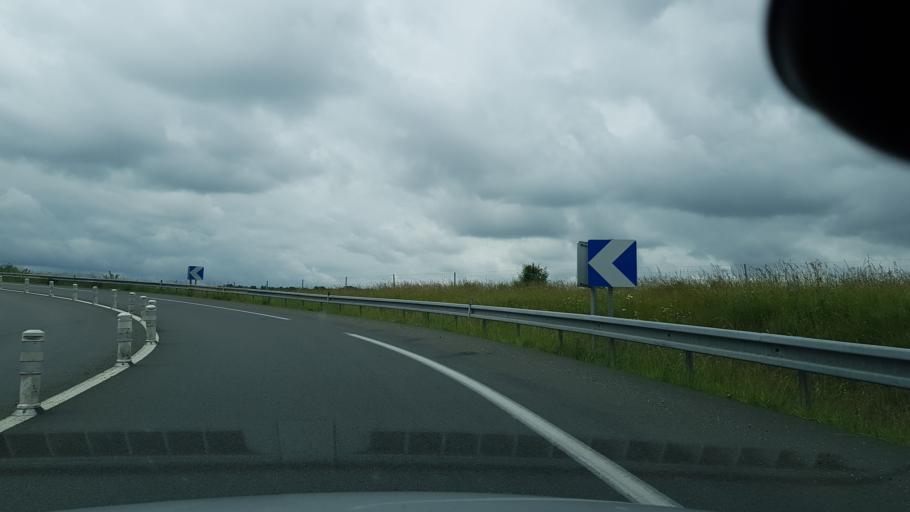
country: FR
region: Centre
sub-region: Departement d'Indre-et-Loire
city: Auzouer-en-Touraine
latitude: 47.5470
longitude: 0.9845
